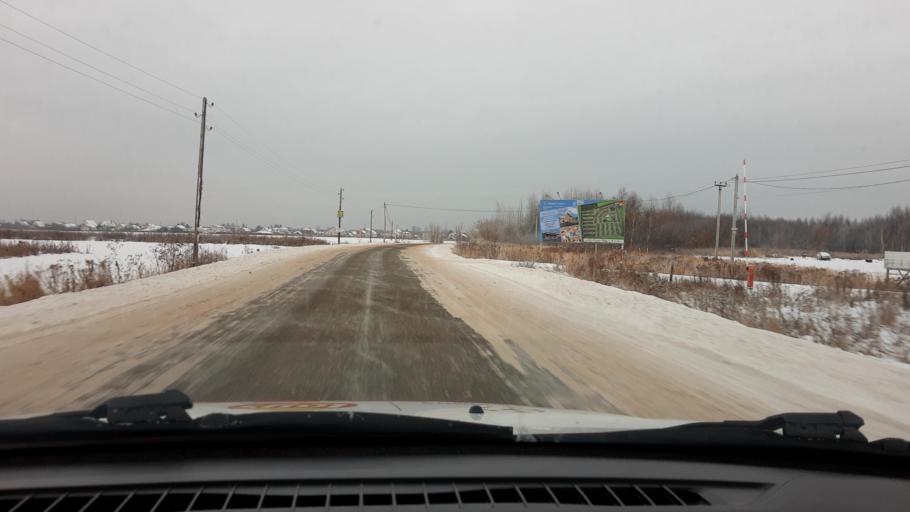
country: RU
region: Nizjnij Novgorod
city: Linda
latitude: 56.5441
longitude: 44.0340
